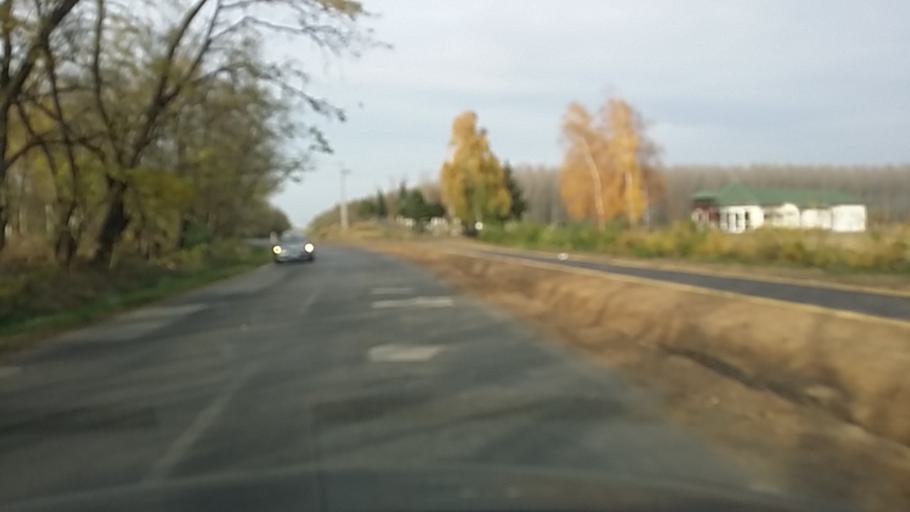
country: HU
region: Szabolcs-Szatmar-Bereg
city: Nyirbogdany
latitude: 48.0668
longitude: 21.8607
